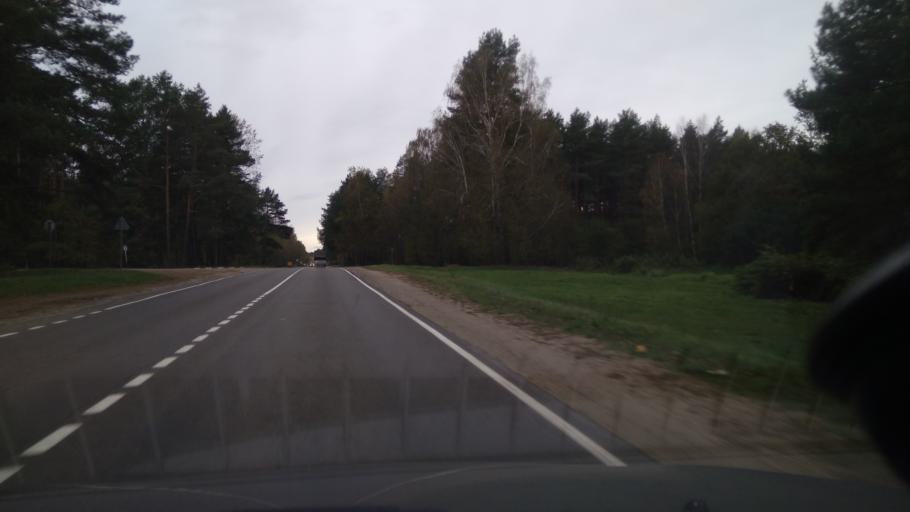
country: BY
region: Minsk
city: Svislach
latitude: 53.6496
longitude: 27.9260
